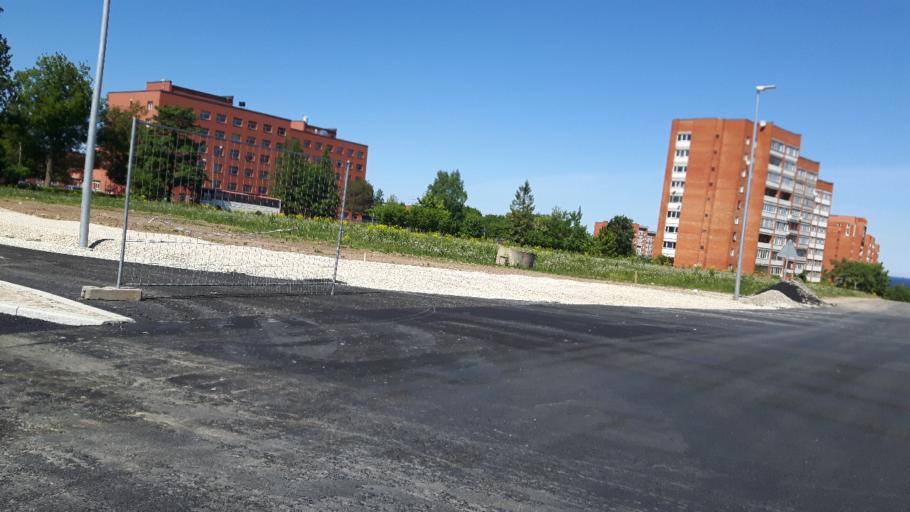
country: EE
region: Ida-Virumaa
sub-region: Sillamaee linn
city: Sillamae
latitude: 59.3894
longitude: 27.7963
